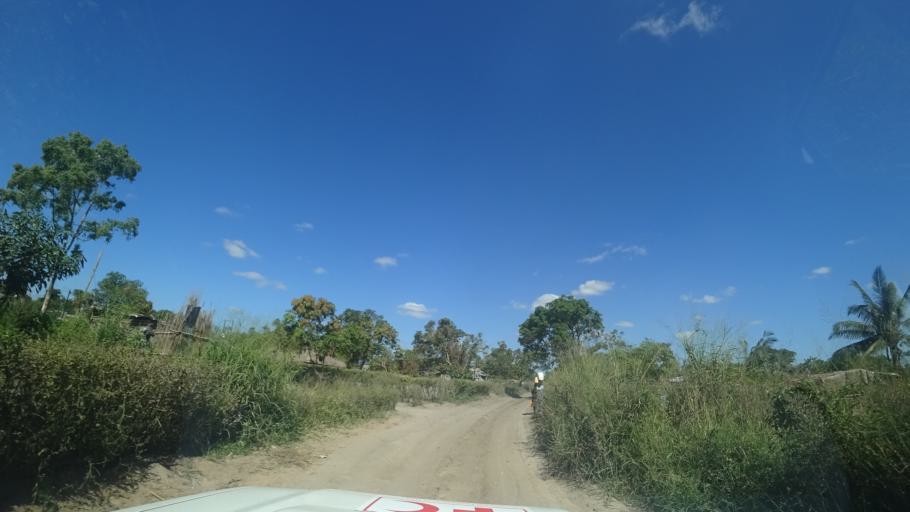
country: MZ
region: Sofala
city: Dondo
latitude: -19.4882
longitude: 34.5994
